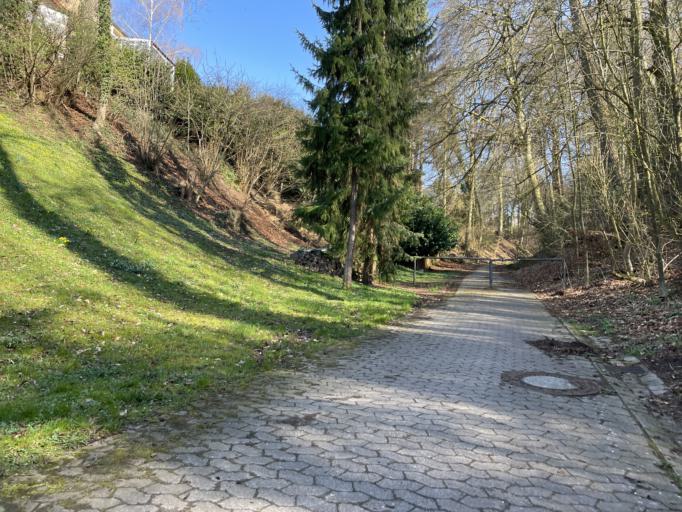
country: DE
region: North Rhine-Westphalia
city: Porta Westfalica
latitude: 52.2365
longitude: 8.9273
